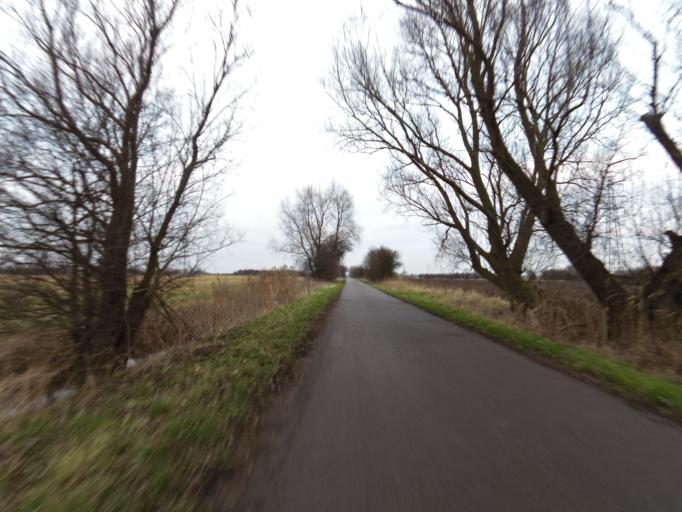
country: GB
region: England
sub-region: Cambridgeshire
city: Bottisham
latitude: 52.2575
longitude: 0.2398
